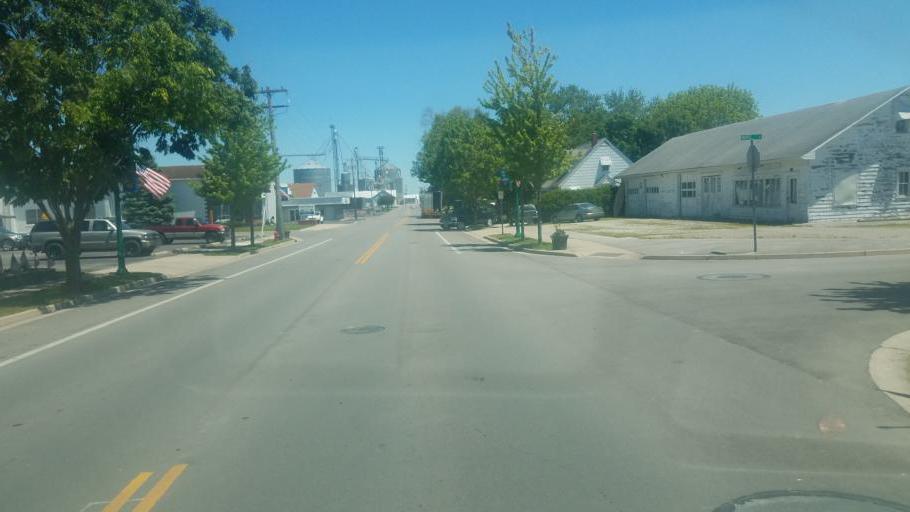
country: US
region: Ohio
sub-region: Darke County
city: Versailles
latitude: 40.2232
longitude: -84.4757
